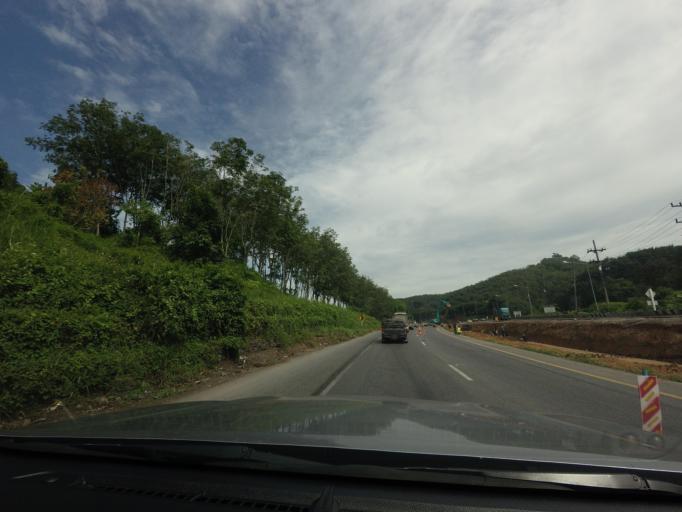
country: TH
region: Nakhon Si Thammarat
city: Ron Phibun
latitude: 8.1413
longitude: 99.7736
